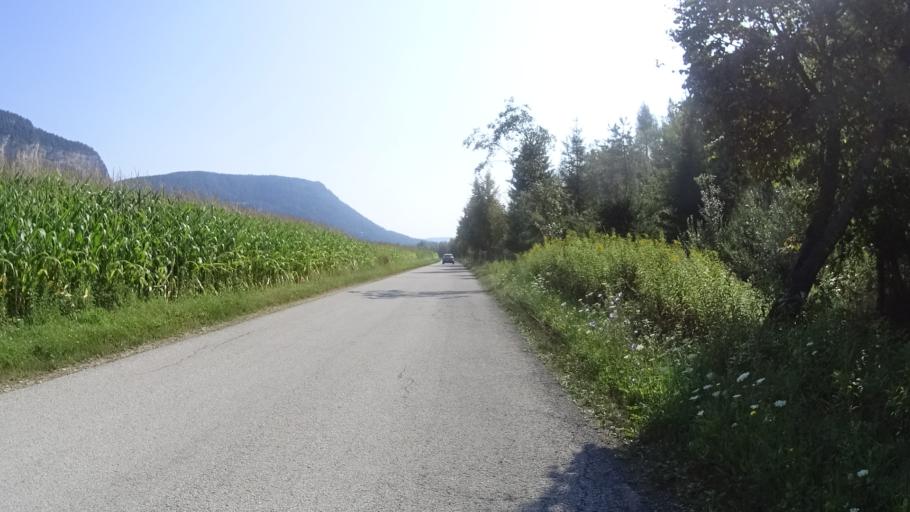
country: AT
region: Carinthia
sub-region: Politischer Bezirk Klagenfurt Land
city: Grafenstein
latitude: 46.5605
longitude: 14.4433
